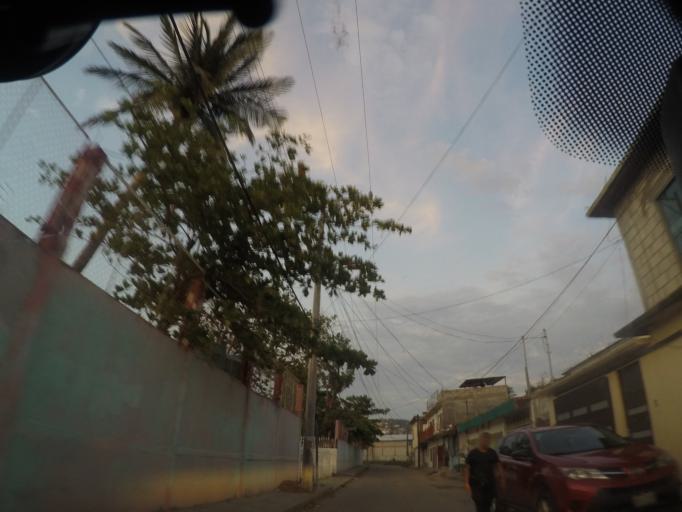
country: MX
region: Oaxaca
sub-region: Salina Cruz
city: Salina Cruz
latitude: 16.1769
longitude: -95.1959
